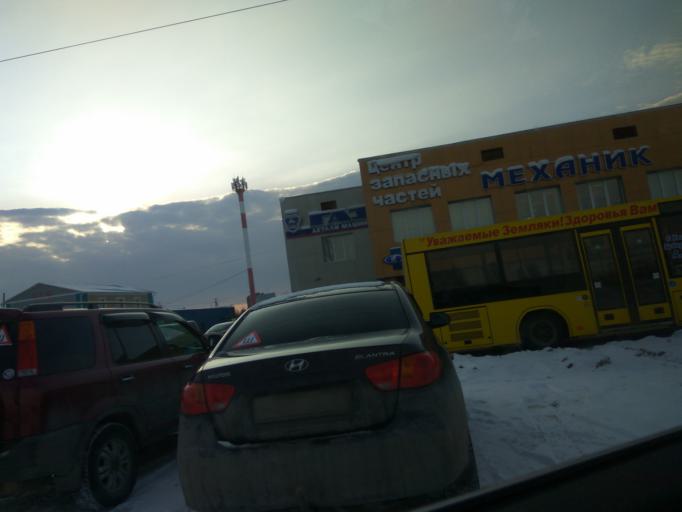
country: RU
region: Kemerovo
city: Yurga
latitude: 55.7137
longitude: 84.9025
